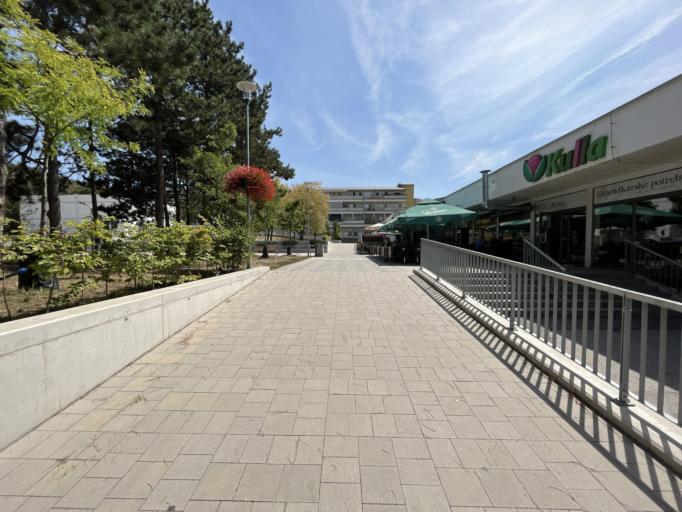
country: SK
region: Bratislavsky
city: Bratislava
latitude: 48.1948
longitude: 17.0514
